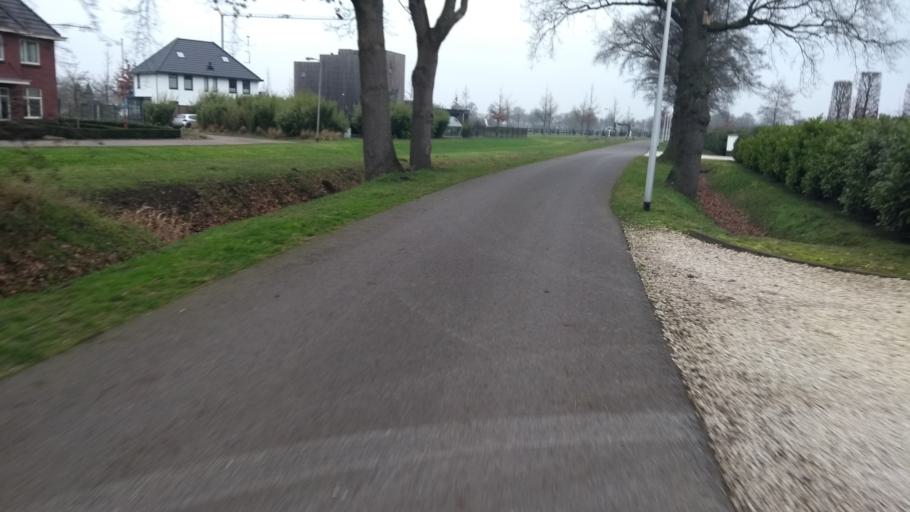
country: NL
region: Overijssel
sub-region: Gemeente Almelo
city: Almelo
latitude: 52.3809
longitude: 6.6934
